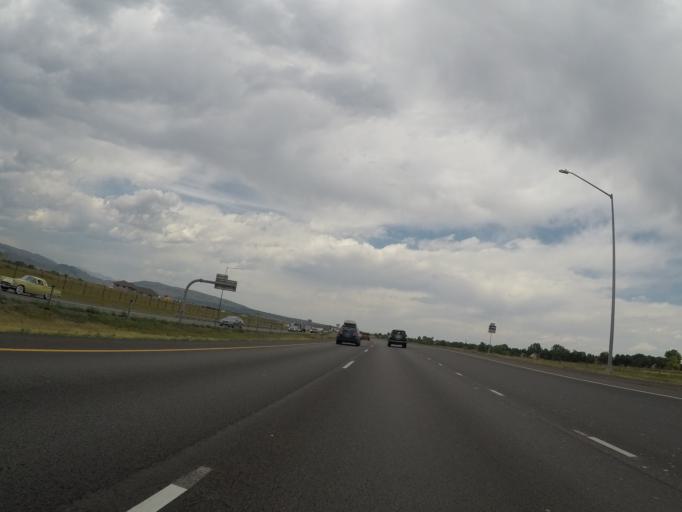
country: US
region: Colorado
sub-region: Jefferson County
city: Ken Caryl
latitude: 39.6132
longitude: -105.1505
